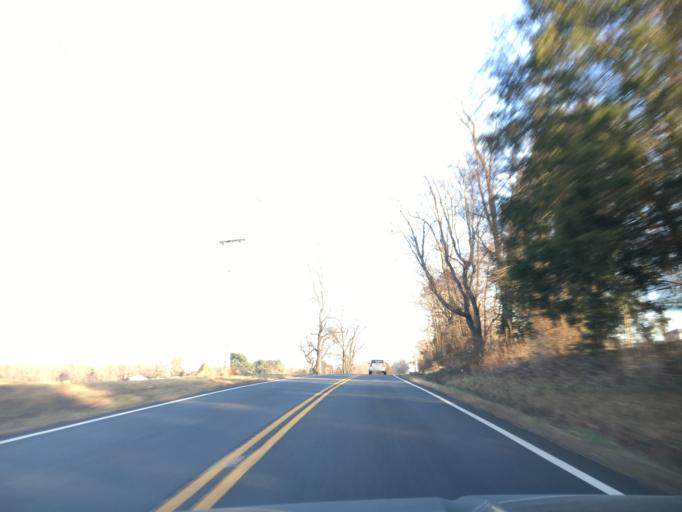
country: US
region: Virginia
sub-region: Culpeper County
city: Merrimac
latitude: 38.5234
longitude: -78.1053
